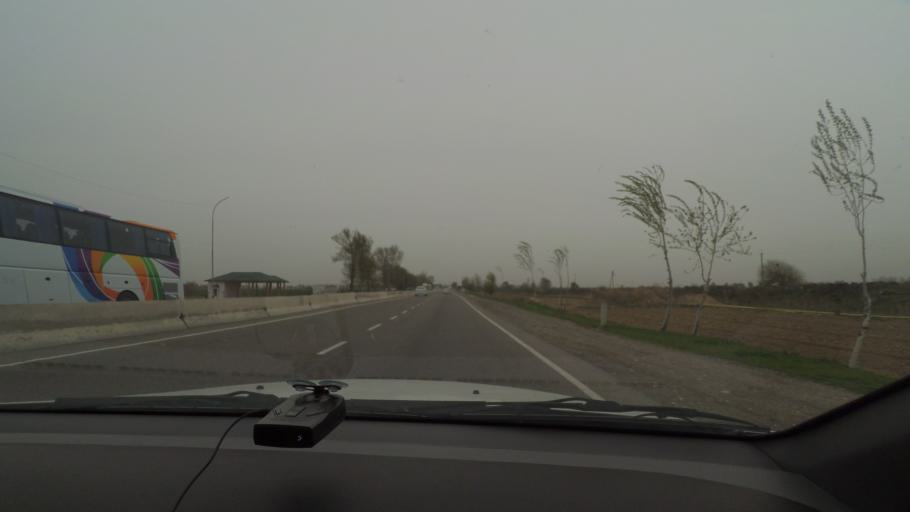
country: KZ
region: Ongtustik Qazaqstan
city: Myrzakent
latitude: 40.5548
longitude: 68.3649
